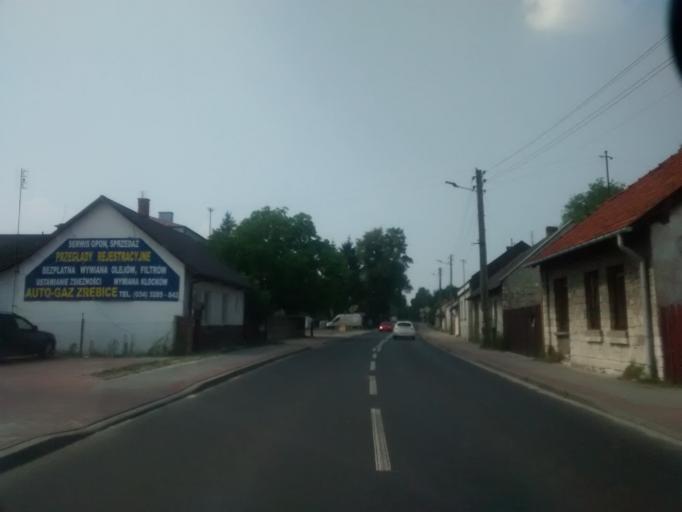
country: PL
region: Silesian Voivodeship
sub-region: Powiat czestochowski
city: Potok Zloty
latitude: 50.7226
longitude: 19.4339
